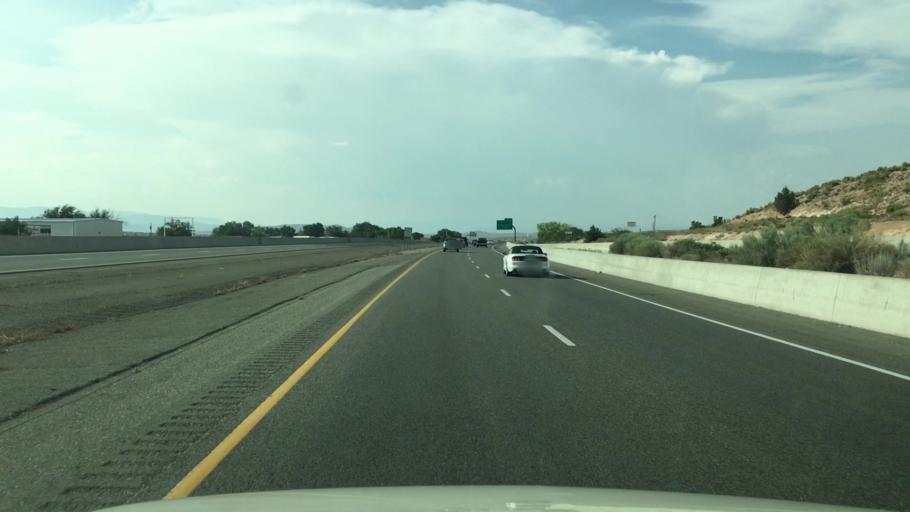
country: US
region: New Mexico
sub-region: Santa Fe County
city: Nambe
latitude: 35.8463
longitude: -105.9935
